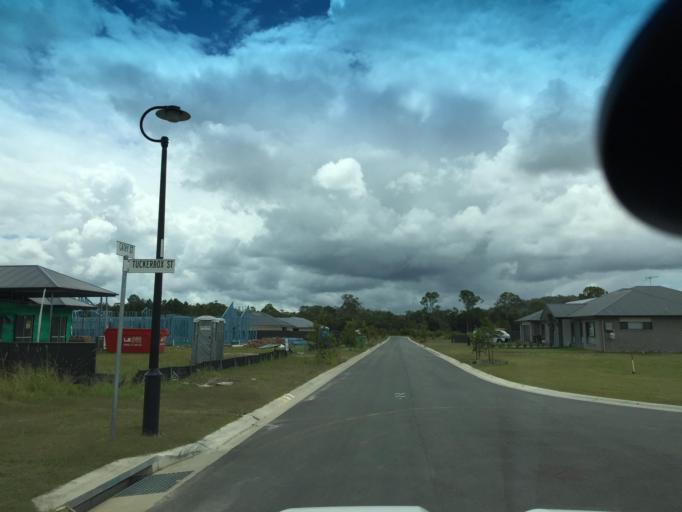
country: AU
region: Queensland
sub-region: Moreton Bay
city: Caboolture
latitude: -27.0421
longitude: 152.9262
